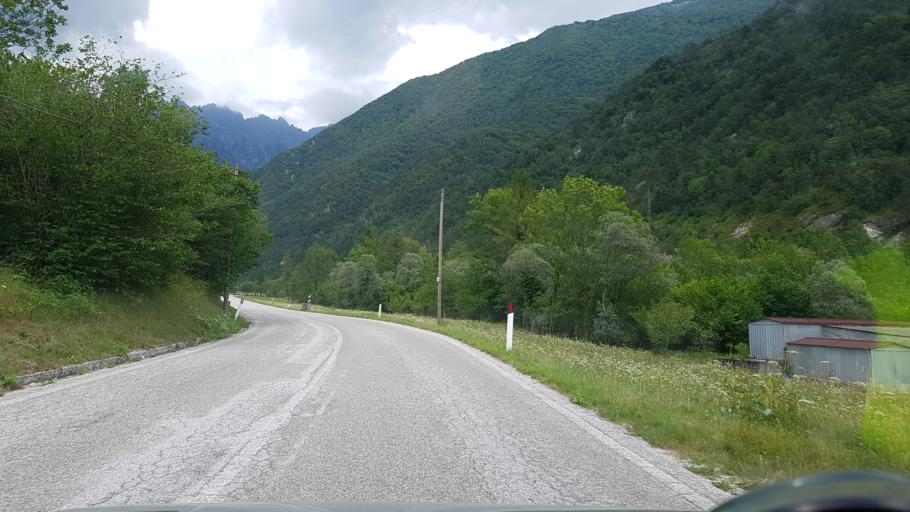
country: IT
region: Friuli Venezia Giulia
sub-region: Provincia di Udine
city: Lusevera
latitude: 46.2846
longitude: 13.2664
